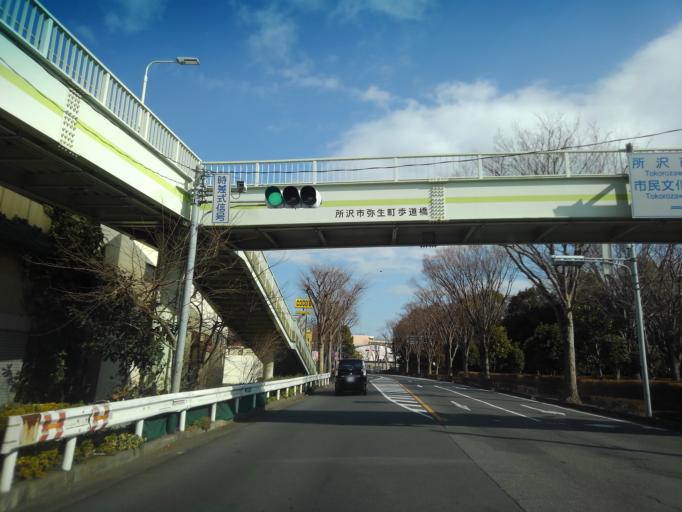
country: JP
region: Saitama
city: Tokorozawa
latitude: 35.8070
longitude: 139.4608
